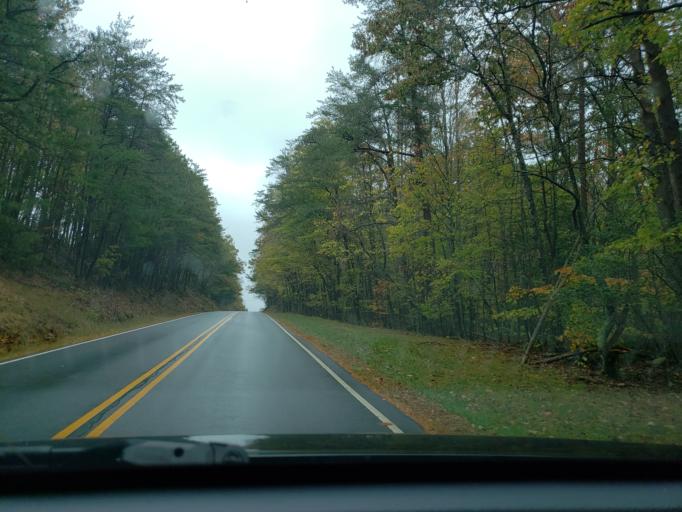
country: US
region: North Carolina
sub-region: Stokes County
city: Danbury
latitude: 36.4141
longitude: -80.2477
